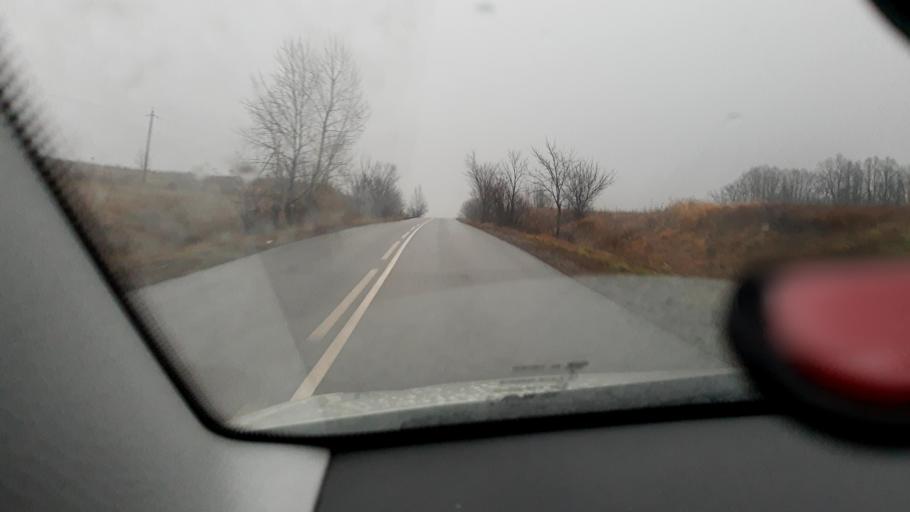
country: RU
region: Bashkortostan
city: Iglino
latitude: 54.8994
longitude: 56.2408
